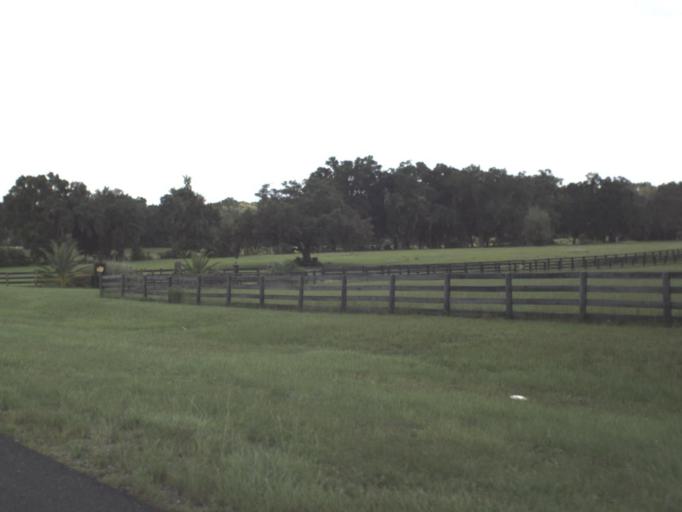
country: US
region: Florida
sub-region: Levy County
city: Williston Highlands
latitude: 29.4062
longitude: -82.5249
